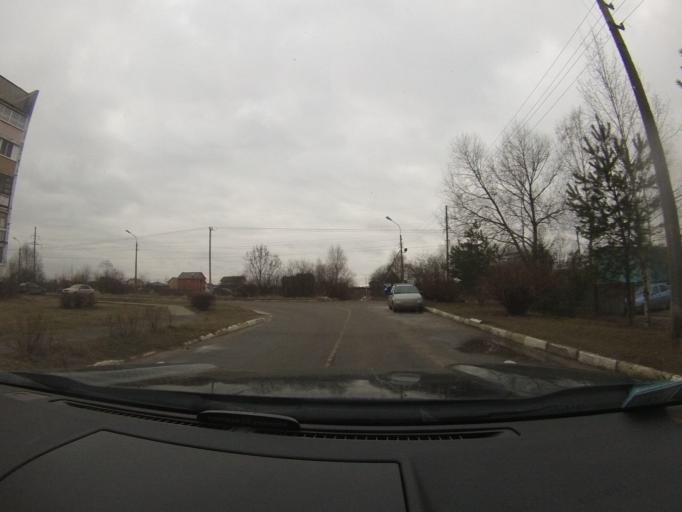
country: RU
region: Moskovskaya
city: Lopatinskiy
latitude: 55.3356
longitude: 38.7077
